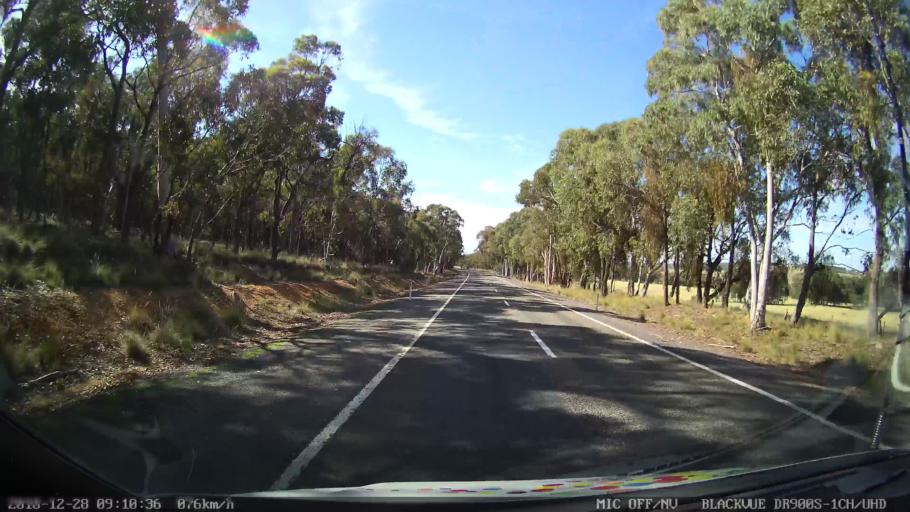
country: AU
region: New South Wales
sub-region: Upper Lachlan Shire
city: Crookwell
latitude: -34.2337
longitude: 149.3368
